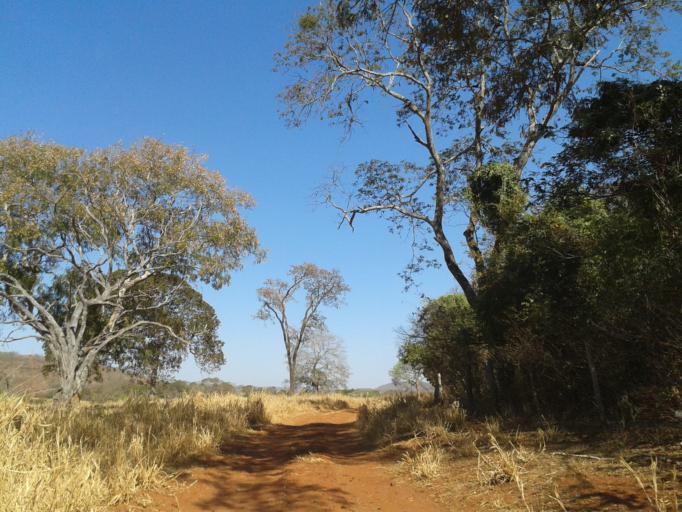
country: BR
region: Minas Gerais
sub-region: Santa Vitoria
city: Santa Vitoria
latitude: -19.1353
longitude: -50.0395
